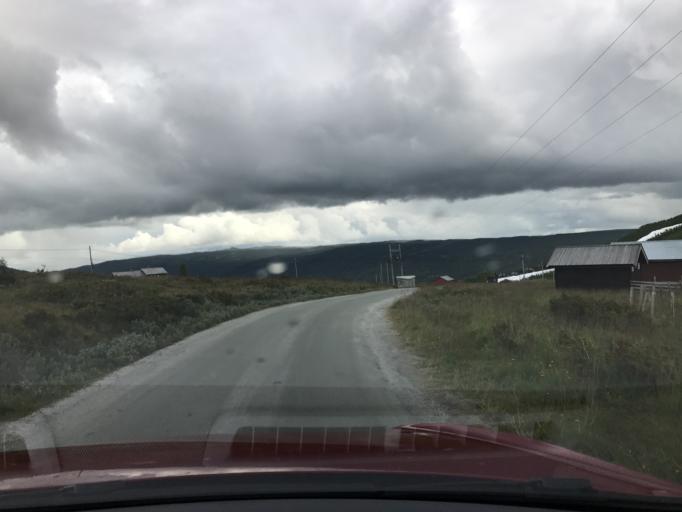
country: NO
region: Buskerud
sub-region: Hol
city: Geilo
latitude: 60.5478
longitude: 8.1829
